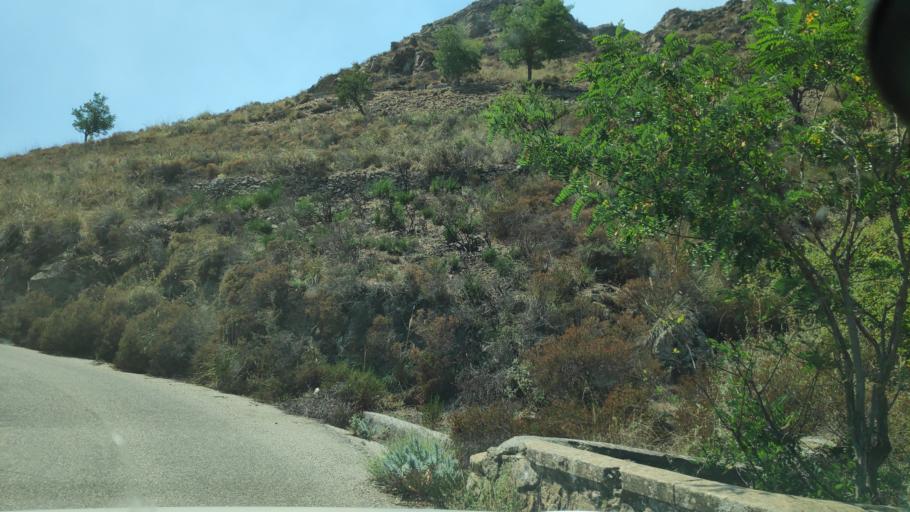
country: IT
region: Calabria
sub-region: Provincia di Reggio Calabria
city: Bova
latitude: 38.0011
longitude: 15.9262
